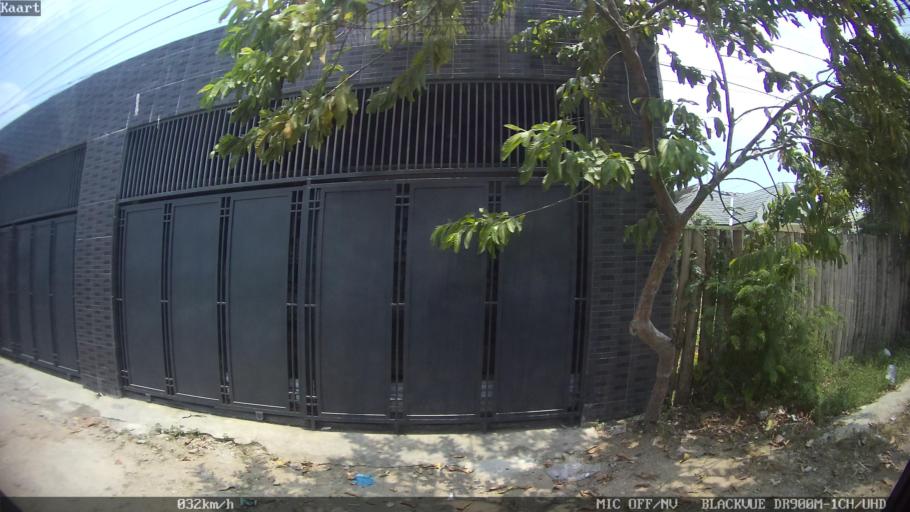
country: ID
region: Lampung
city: Pringsewu
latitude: -5.3508
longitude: 104.9671
